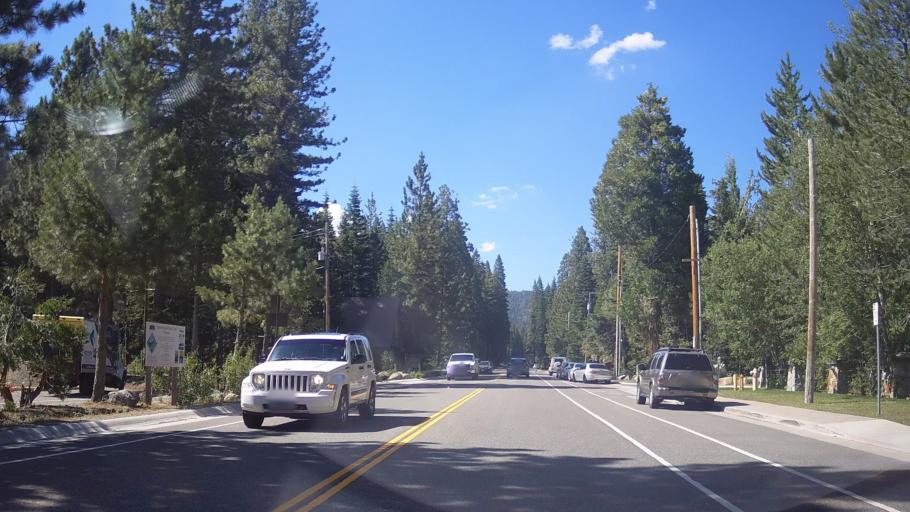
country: US
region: California
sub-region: Placer County
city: Tahoma
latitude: 39.0865
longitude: -120.1606
